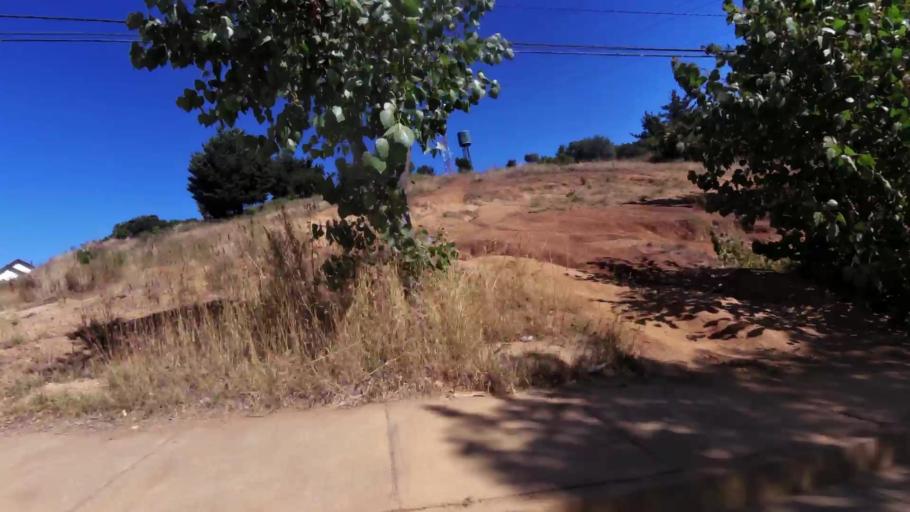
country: CL
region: Biobio
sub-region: Provincia de Concepcion
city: Concepcion
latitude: -36.7918
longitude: -73.0509
